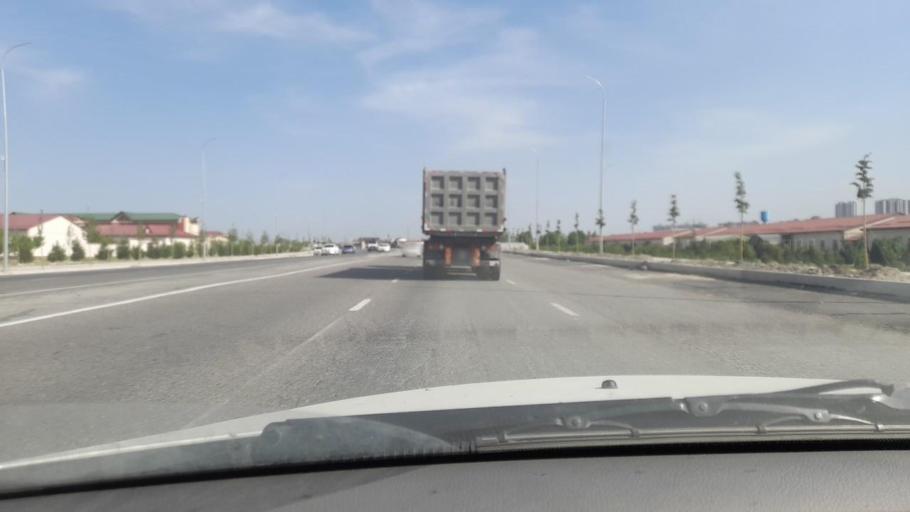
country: UZ
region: Samarqand
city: Daxbet
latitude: 39.7326
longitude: 66.9351
